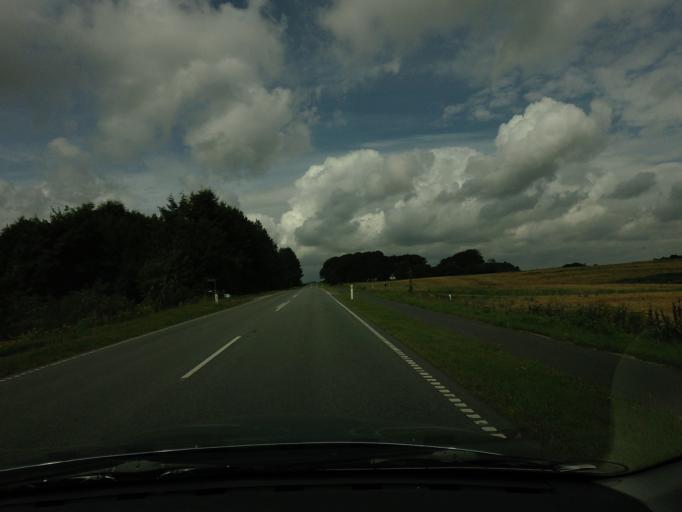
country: DK
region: North Denmark
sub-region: Hjorring Kommune
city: Tars
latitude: 57.3798
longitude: 10.1430
